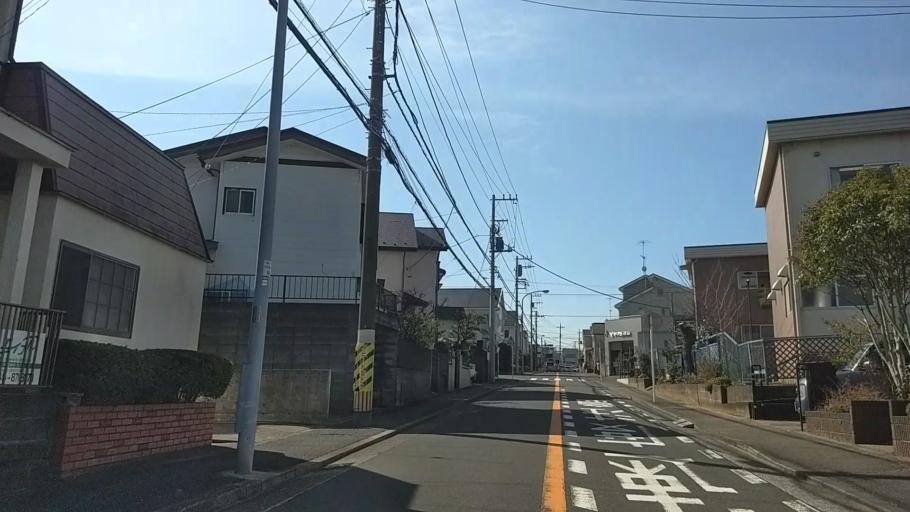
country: JP
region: Kanagawa
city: Kamakura
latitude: 35.3942
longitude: 139.5568
